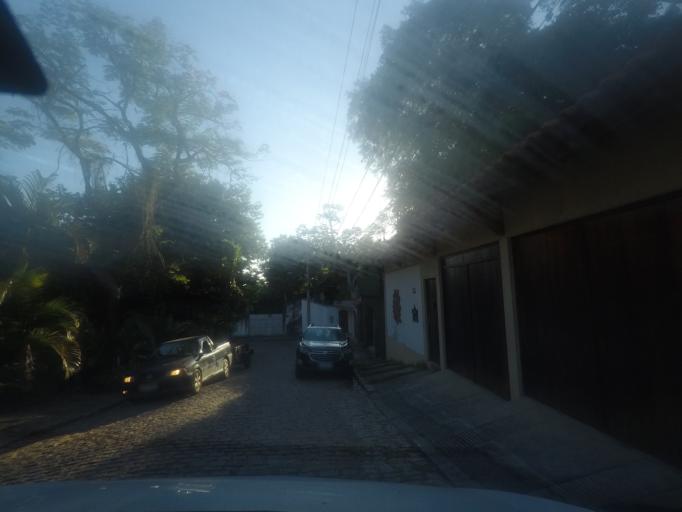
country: BR
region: Rio de Janeiro
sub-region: Rio De Janeiro
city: Rio de Janeiro
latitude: -22.9316
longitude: -43.1886
